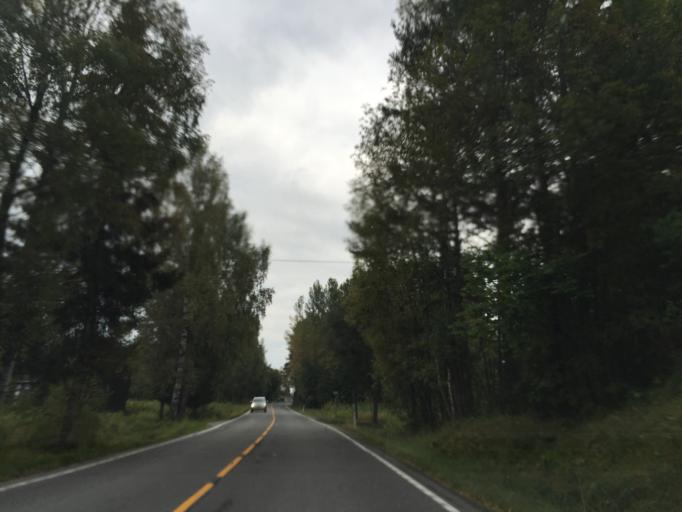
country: NO
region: Hedmark
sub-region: Loten
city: Loten
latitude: 60.6695
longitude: 11.3745
